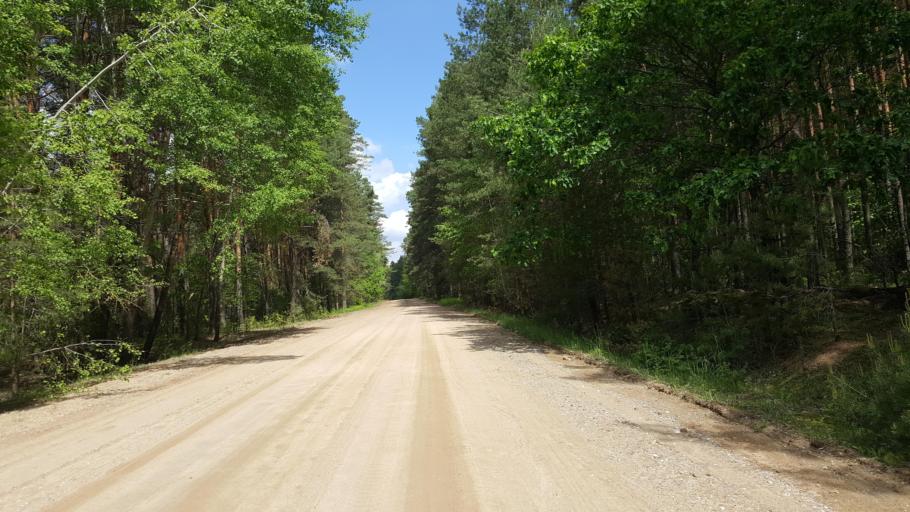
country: BY
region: Brest
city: Kamyanyets
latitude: 52.4679
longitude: 23.9675
